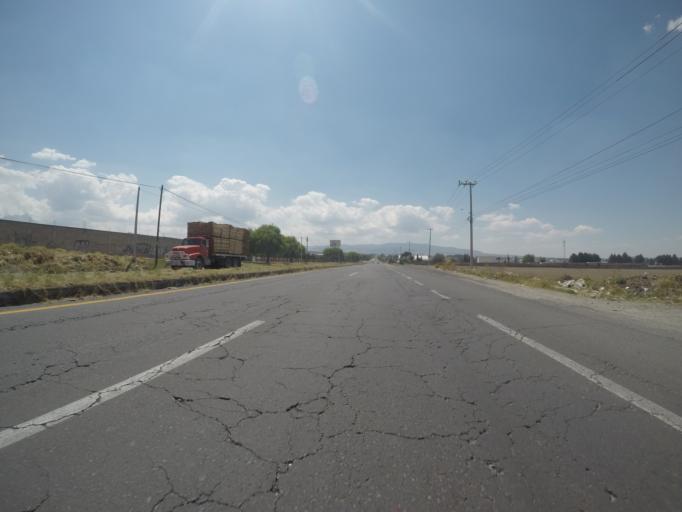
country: MX
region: Mexico
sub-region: Toluca
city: San Antonio Buenavista
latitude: 19.2556
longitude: -99.7175
